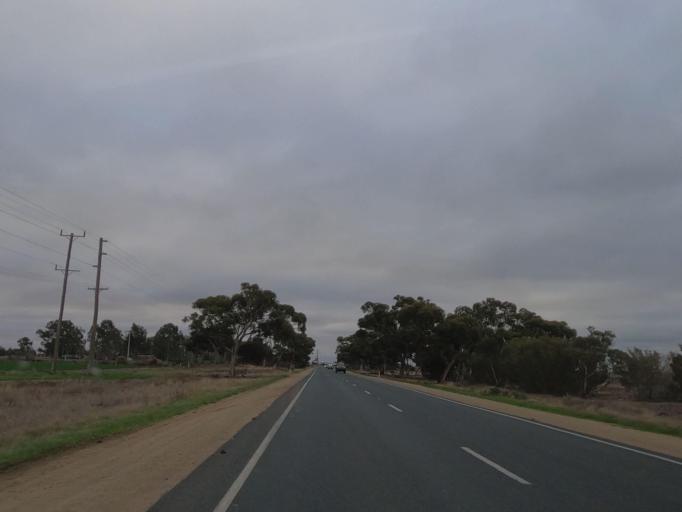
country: AU
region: Victoria
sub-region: Swan Hill
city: Swan Hill
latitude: -35.3984
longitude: 143.5753
